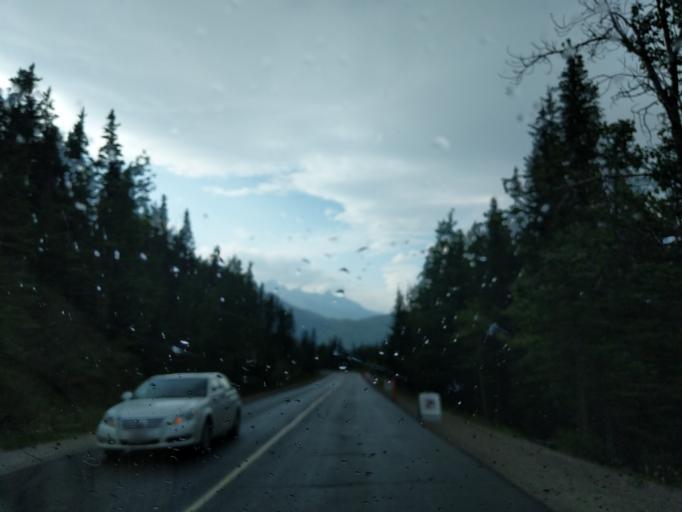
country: CA
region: Alberta
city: Banff
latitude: 51.1580
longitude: -115.5651
